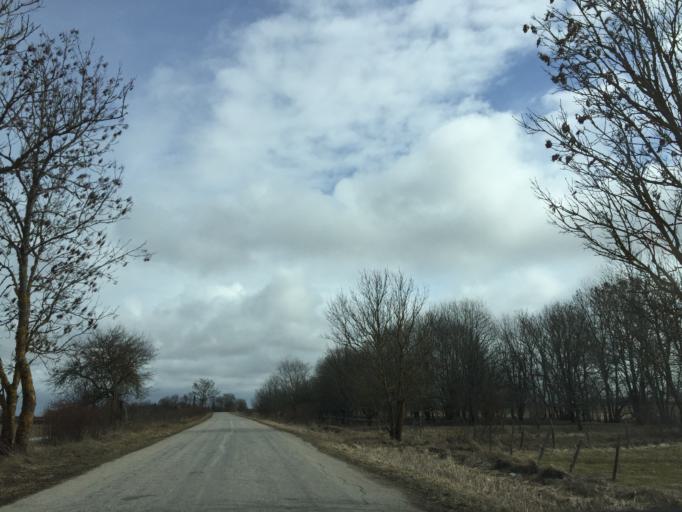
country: EE
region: Laeaene
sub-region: Lihula vald
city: Lihula
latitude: 58.7359
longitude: 23.8379
